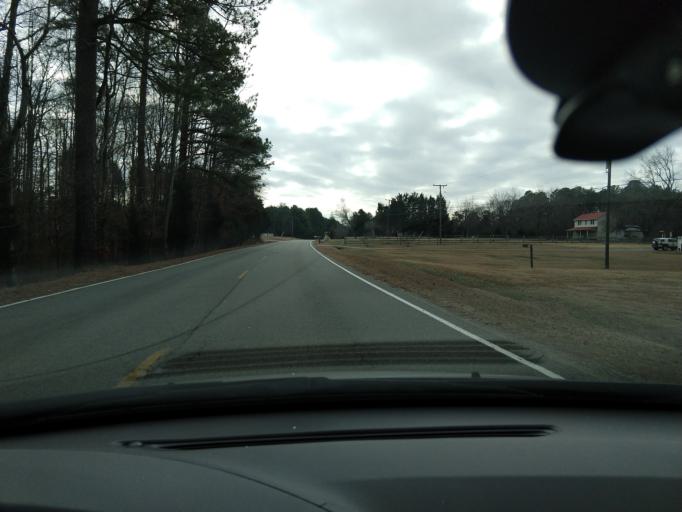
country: US
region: Virginia
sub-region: Henrico County
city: Fort Lee
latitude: 37.4357
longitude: -77.3666
